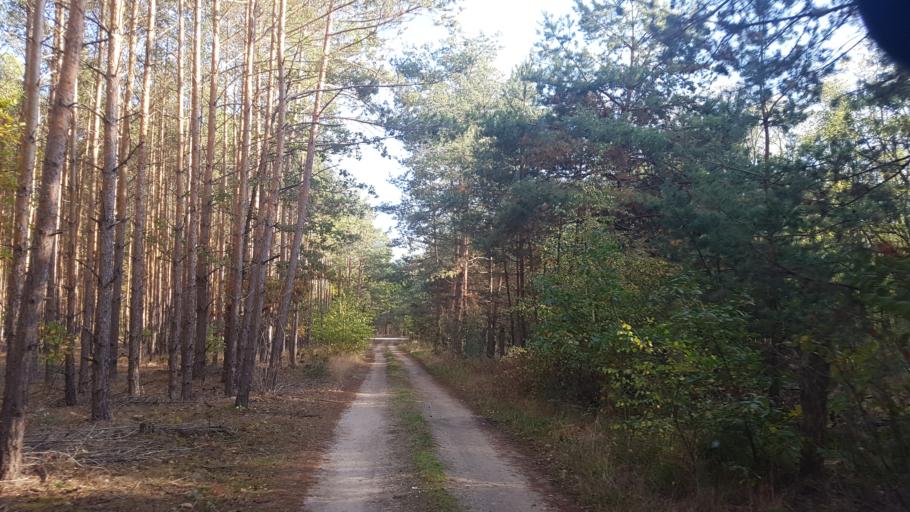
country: DE
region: Brandenburg
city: Schonewalde
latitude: 51.6526
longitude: 13.6214
